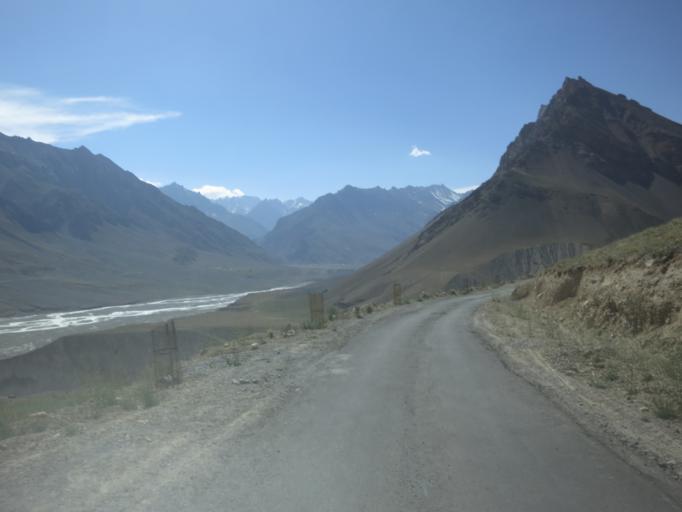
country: IN
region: Himachal Pradesh
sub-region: Shimla
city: Sarahan
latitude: 32.3030
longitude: 78.0056
